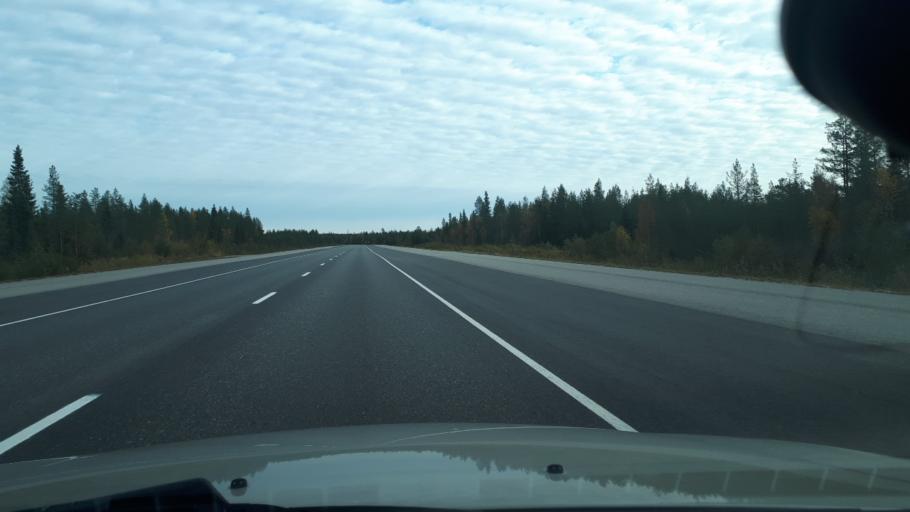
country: FI
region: Northern Ostrobothnia
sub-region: Oulu
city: Yli-Ii
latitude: 65.8978
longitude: 25.7149
